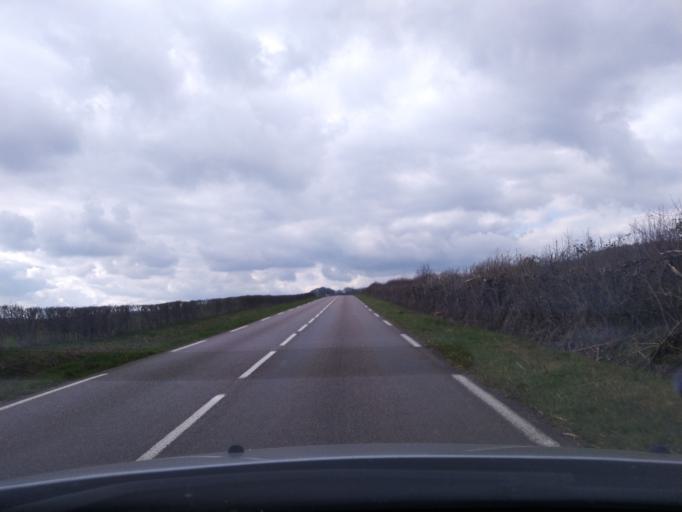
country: FR
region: Bourgogne
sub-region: Departement de l'Yonne
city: Avallon
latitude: 47.5355
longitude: 4.0167
